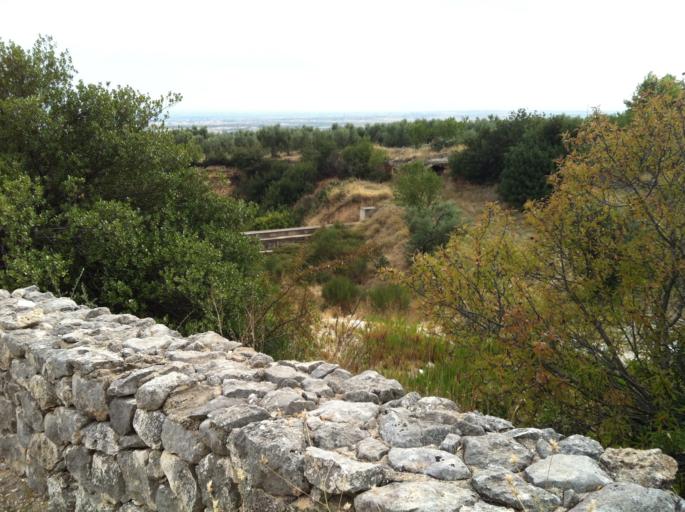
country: IT
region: Apulia
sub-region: Provincia di Foggia
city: Manfredonia
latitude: 41.6641
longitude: 15.9118
